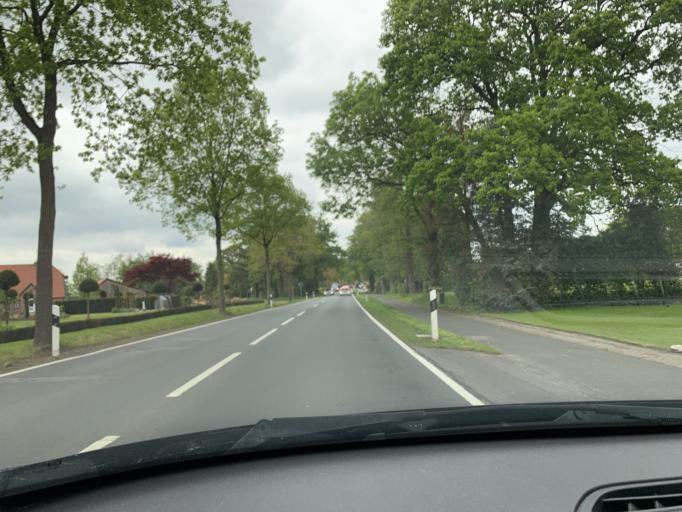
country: DE
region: Lower Saxony
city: Bad Zwischenahn
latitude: 53.2181
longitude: 8.0096
